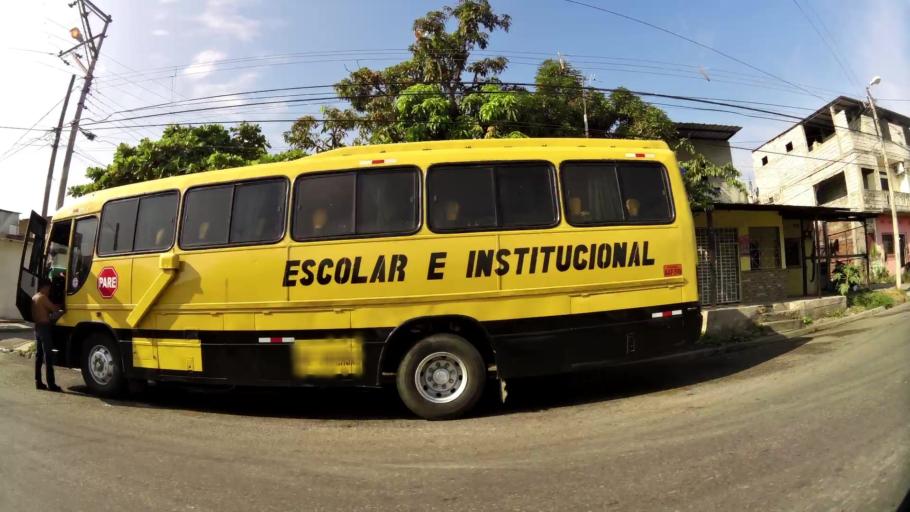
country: EC
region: Guayas
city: Santa Lucia
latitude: -2.0725
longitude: -79.9367
